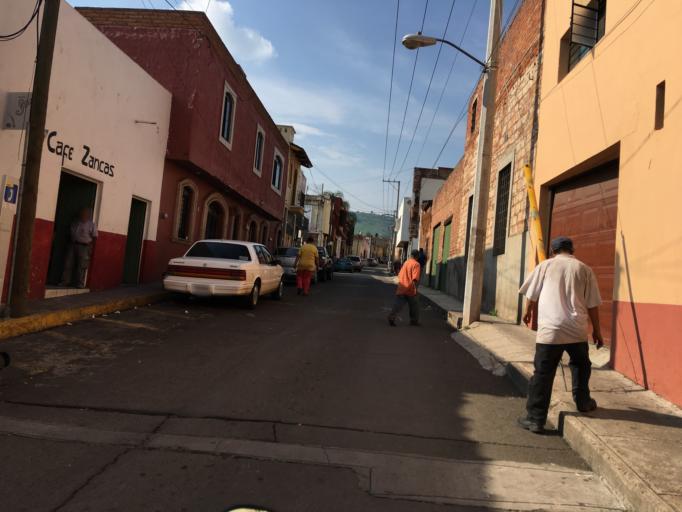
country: MX
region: Jalisco
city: Atotonilco el Alto
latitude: 20.5513
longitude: -102.5096
